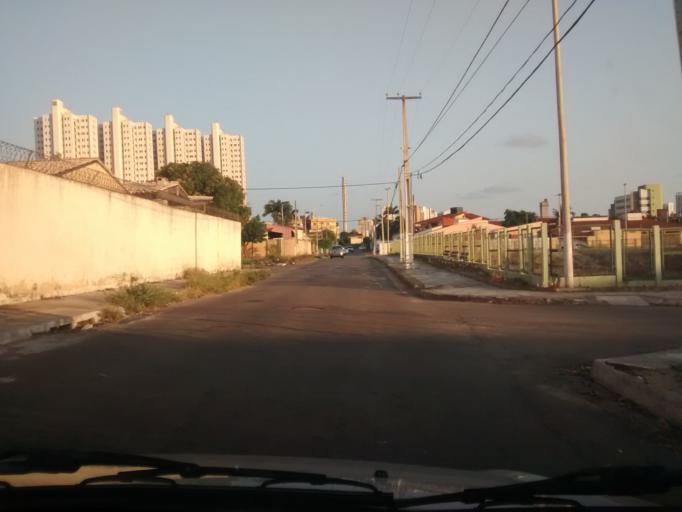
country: BR
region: Rio Grande do Norte
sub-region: Natal
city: Natal
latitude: -5.8661
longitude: -35.1890
